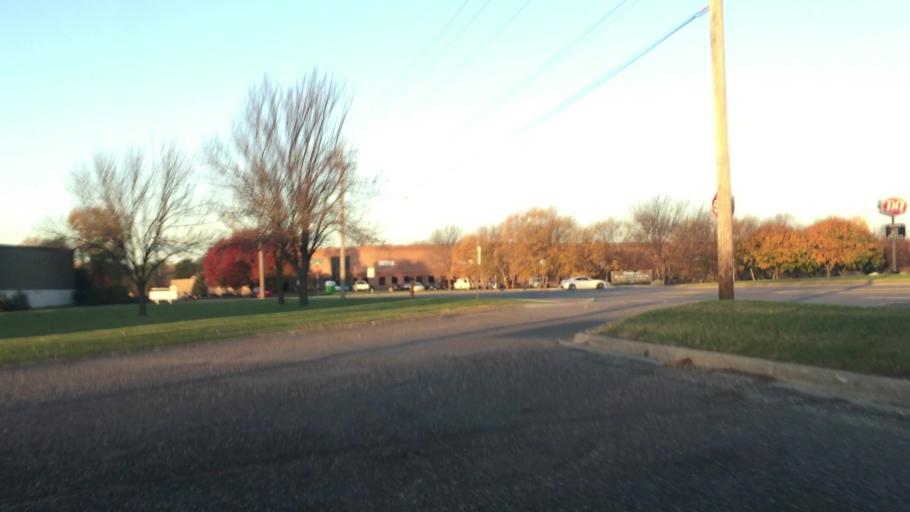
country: US
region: Minnesota
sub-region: Anoka County
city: Fridley
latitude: 45.1065
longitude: -93.2664
